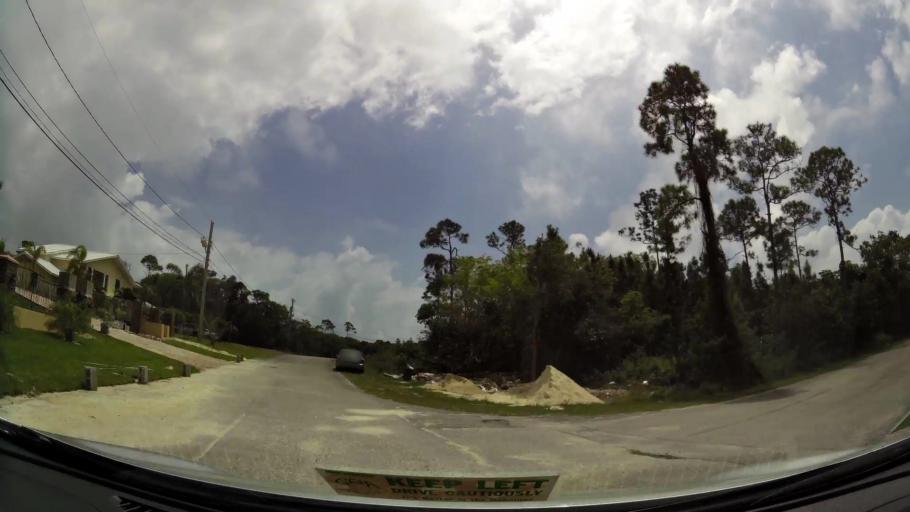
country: BS
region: Freeport
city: Lucaya
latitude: 26.5223
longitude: -78.6503
